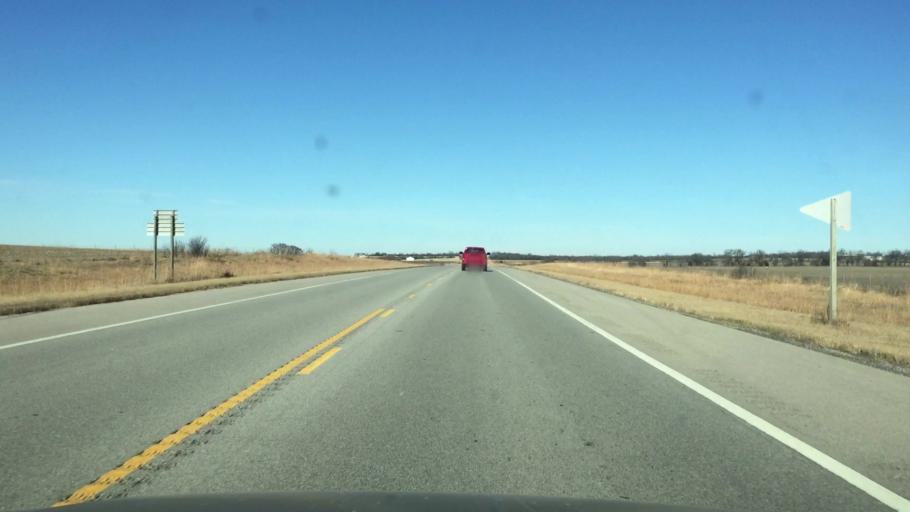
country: US
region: Kansas
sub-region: Allen County
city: Iola
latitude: 37.9528
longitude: -95.3812
